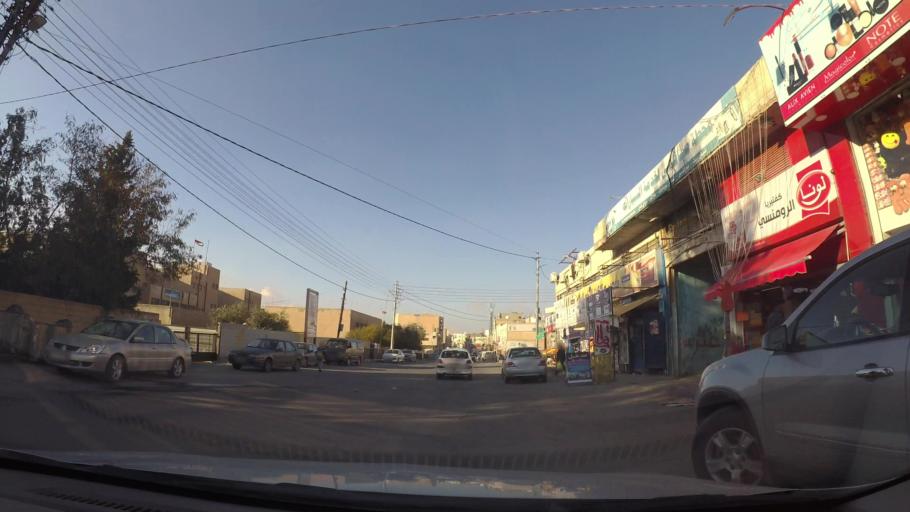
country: JO
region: Amman
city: Al Bunayyat ash Shamaliyah
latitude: 31.9003
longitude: 35.9121
